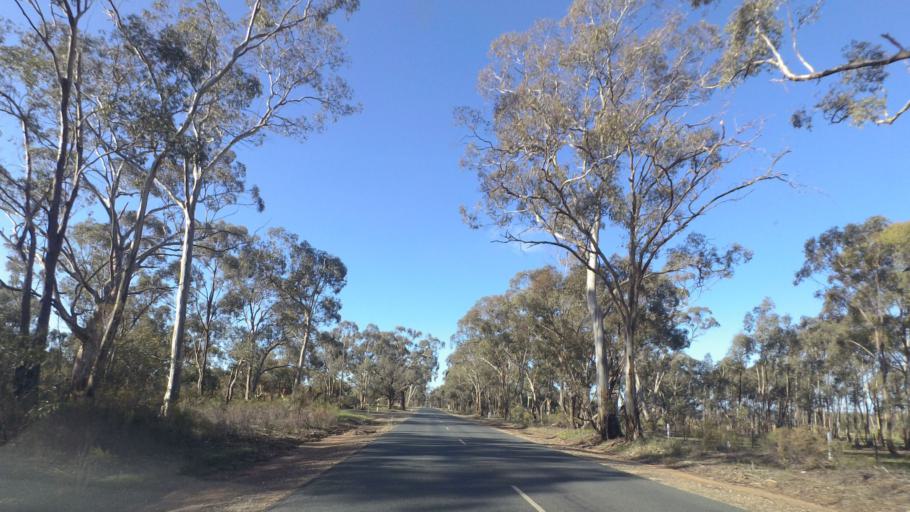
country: AU
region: Victoria
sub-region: Greater Bendigo
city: Epsom
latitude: -36.6628
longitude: 144.4513
